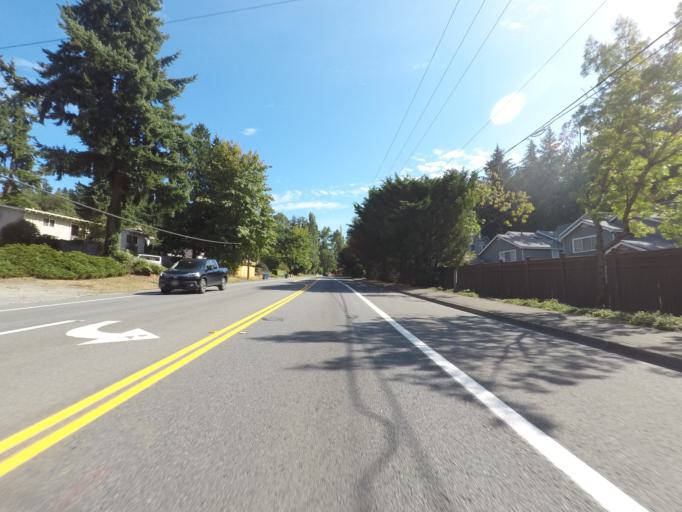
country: US
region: Washington
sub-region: King County
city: Kenmore
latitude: 47.7441
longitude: -122.2498
